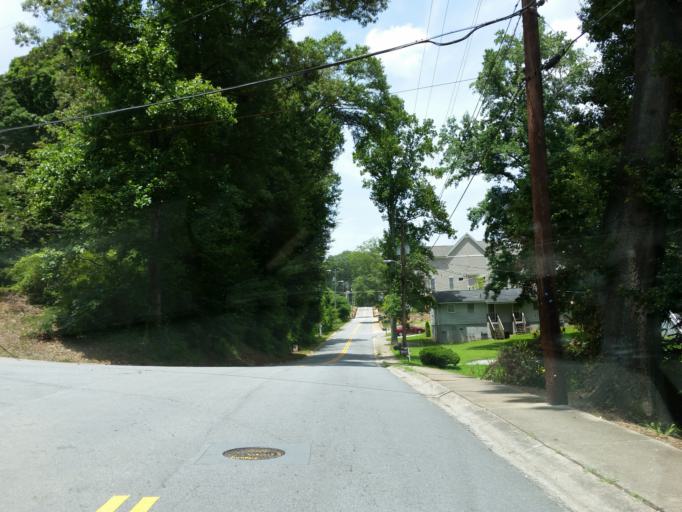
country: US
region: Georgia
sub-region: Cobb County
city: Marietta
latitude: 33.9443
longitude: -84.5398
